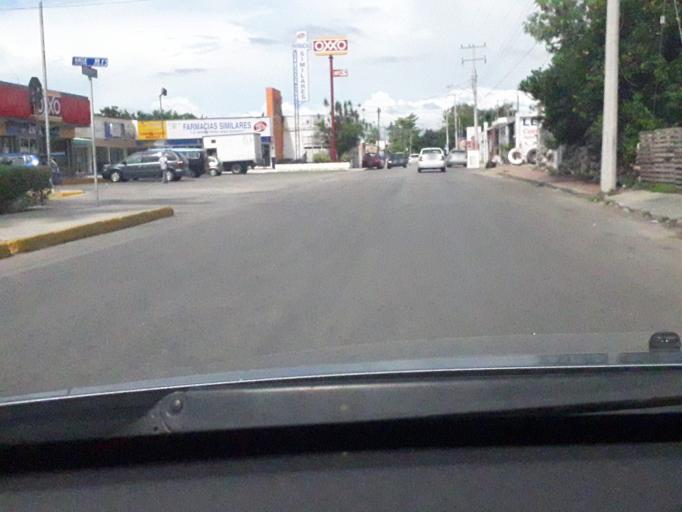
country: MX
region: Yucatan
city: Merida
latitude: 20.9767
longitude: -89.6556
